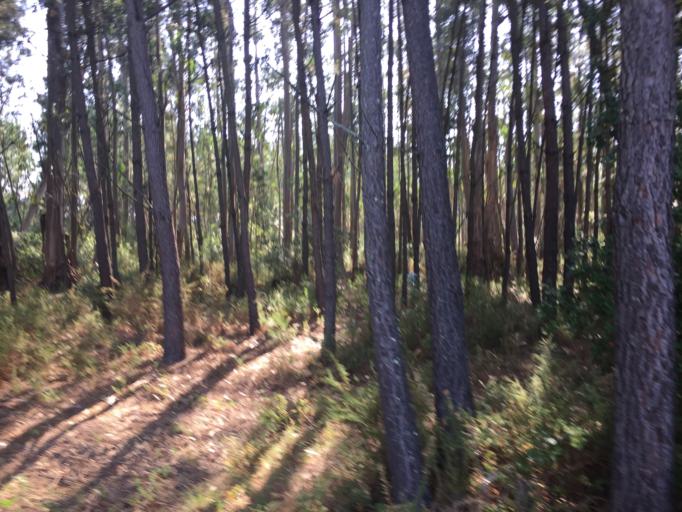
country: PT
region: Coimbra
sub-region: Cantanhede
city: Cantanhede
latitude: 40.4233
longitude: -8.5458
